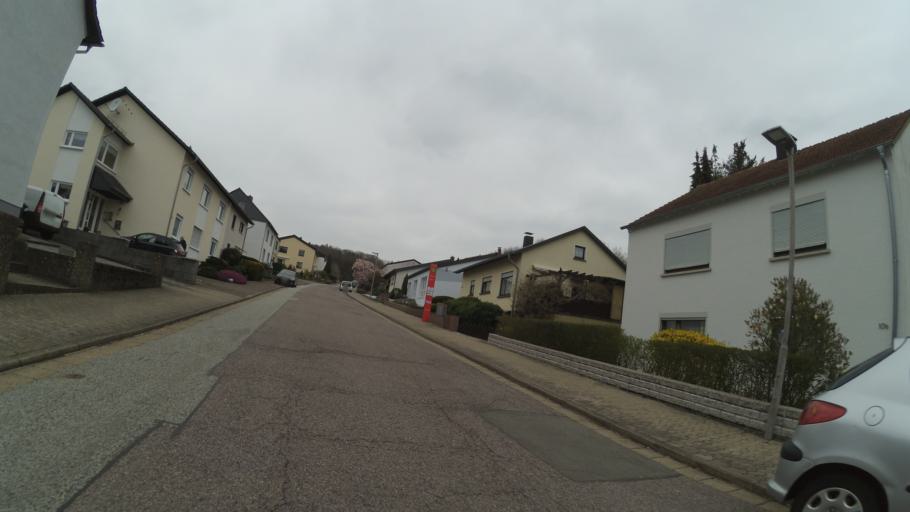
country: DE
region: Saarland
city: Sankt Ingbert
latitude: 49.2898
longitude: 7.0987
